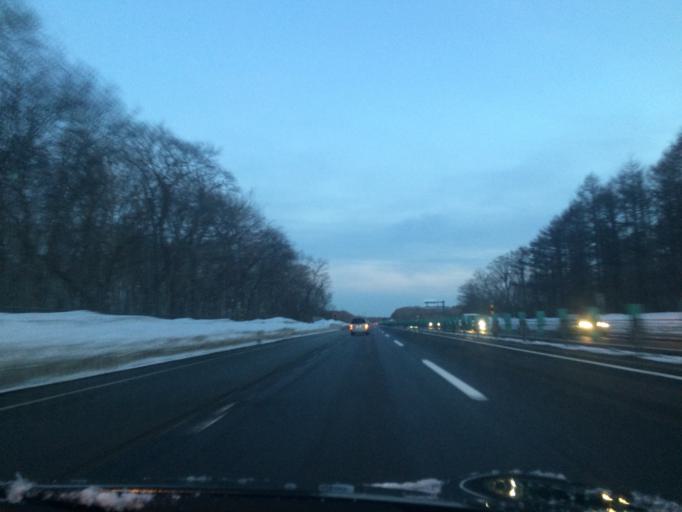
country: JP
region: Hokkaido
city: Chitose
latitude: 42.8097
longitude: 141.6220
